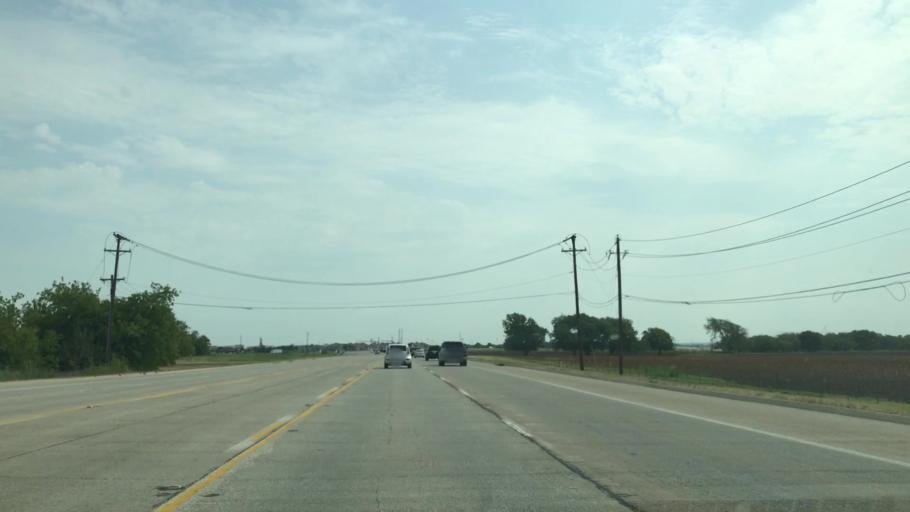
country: US
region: Texas
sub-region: Denton County
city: Roanoke
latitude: 32.9804
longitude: -97.2405
